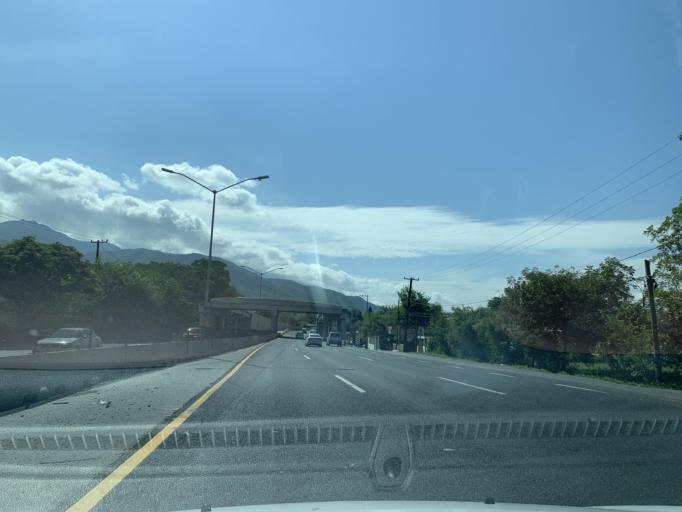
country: MX
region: Nuevo Leon
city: Santiago
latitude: 25.4107
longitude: -100.1387
